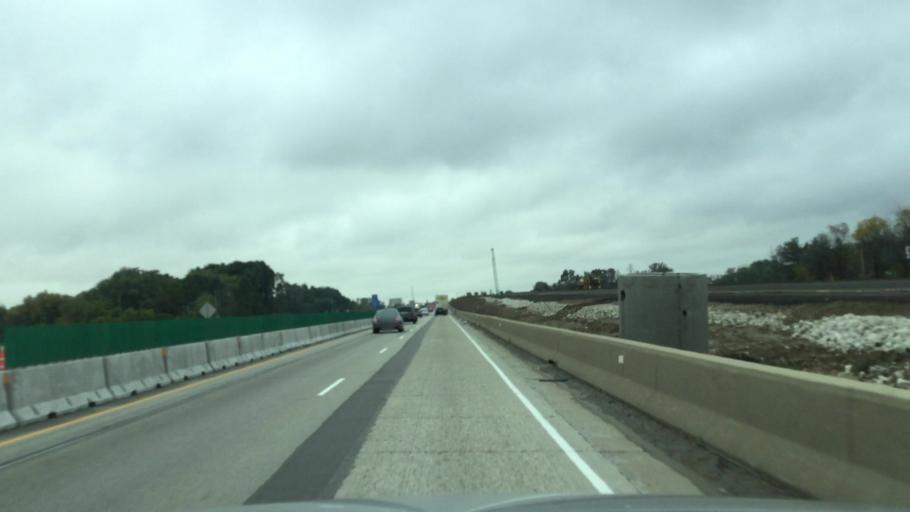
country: US
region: Wisconsin
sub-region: Kenosha County
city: Somers
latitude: 42.6645
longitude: -87.9528
